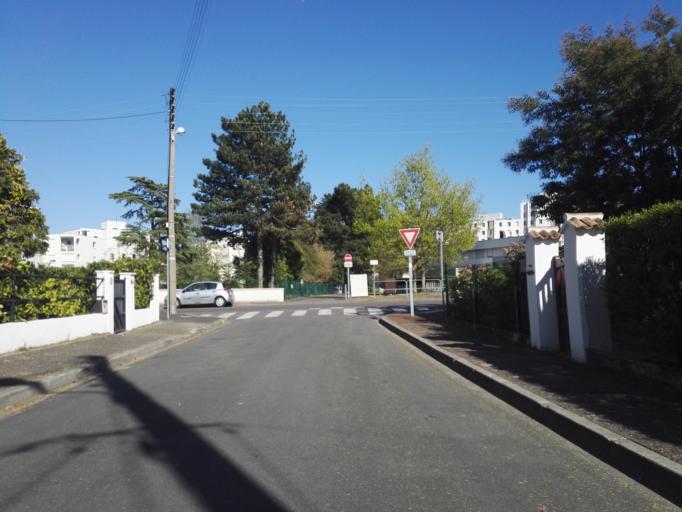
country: FR
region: Aquitaine
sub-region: Departement de la Gironde
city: Talence
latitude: 44.7948
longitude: -0.5870
